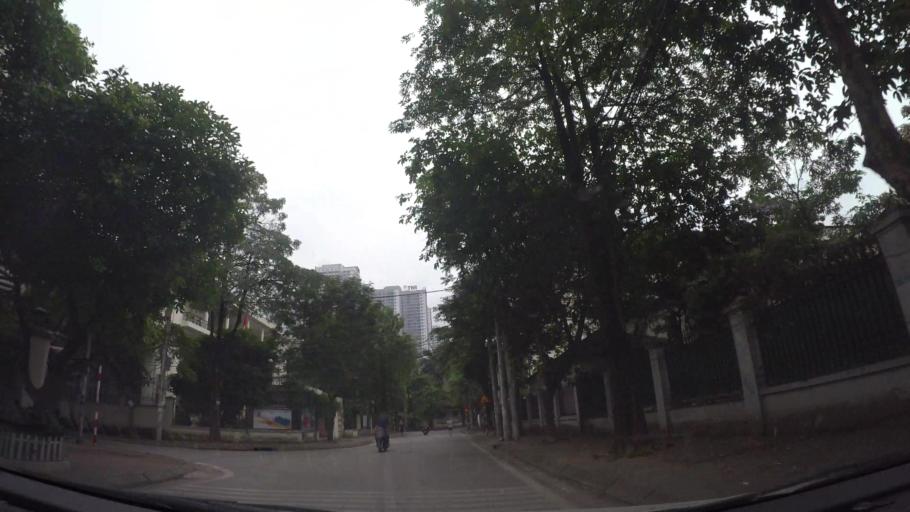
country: VN
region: Ha Noi
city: Cau Dien
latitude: 21.0383
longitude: 105.7660
